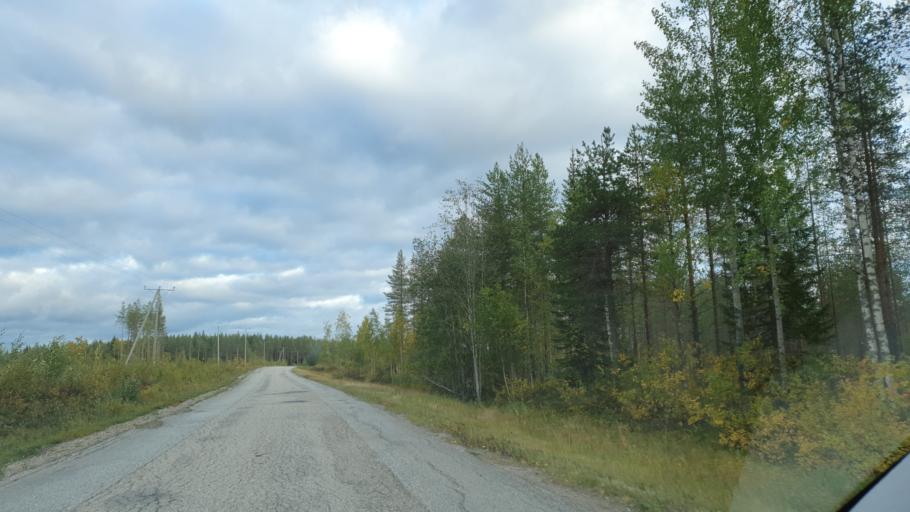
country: FI
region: North Karelia
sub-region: Pielisen Karjala
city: Lieksa
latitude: 63.9155
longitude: 30.1767
